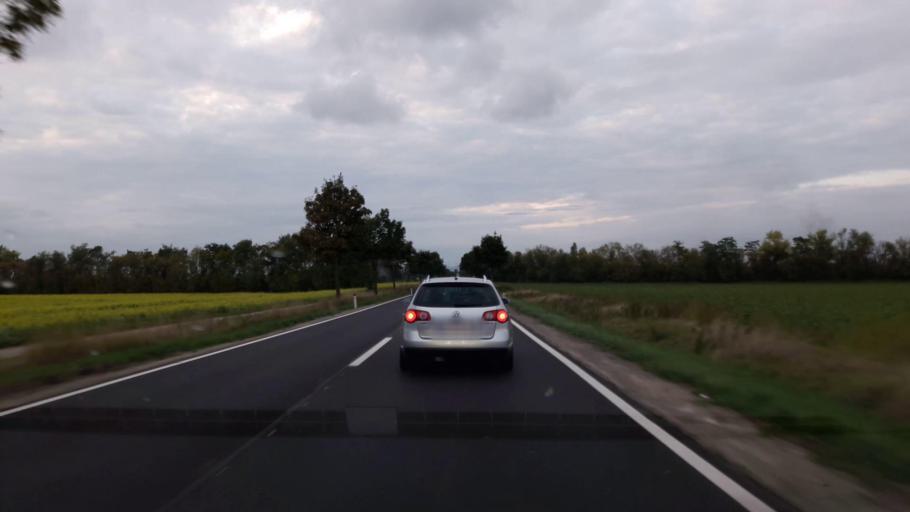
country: AT
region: Lower Austria
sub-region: Politischer Bezirk Wien-Umgebung
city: Rauchenwarth
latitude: 48.1122
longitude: 16.5226
